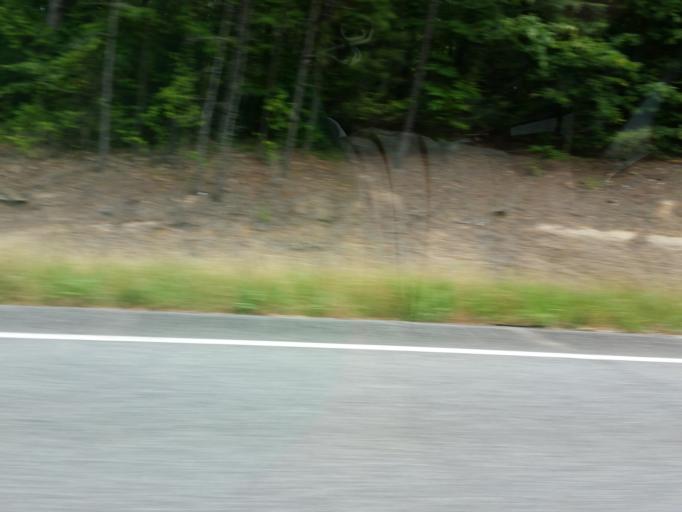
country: US
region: Alabama
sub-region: Sumter County
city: York
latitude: 32.3616
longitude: -88.1899
